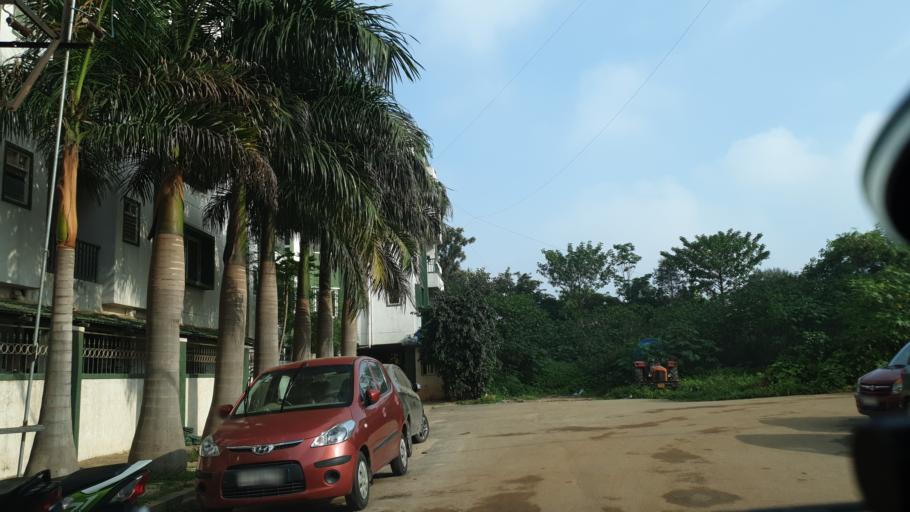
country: IN
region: Karnataka
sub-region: Bangalore Urban
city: Bangalore
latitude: 12.9595
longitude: 77.7084
